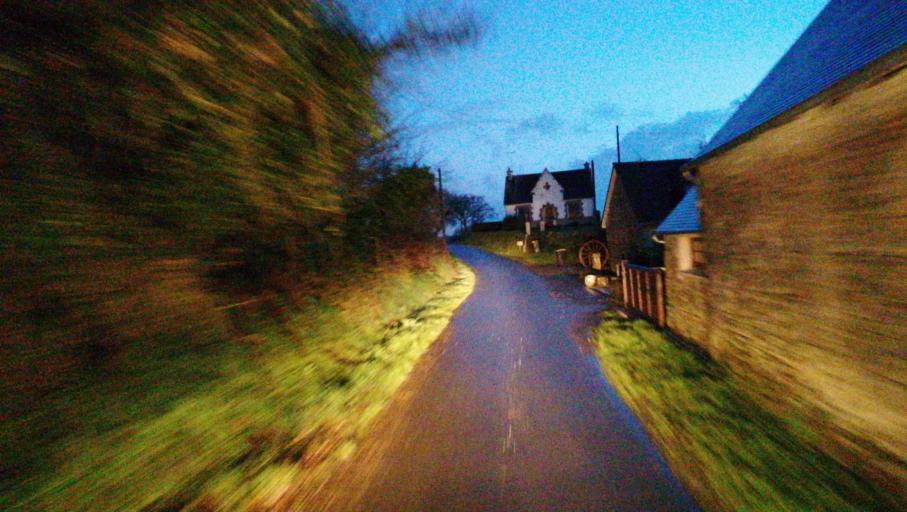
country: FR
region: Brittany
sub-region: Departement des Cotes-d'Armor
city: Plehedel
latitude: 48.6675
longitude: -3.0517
